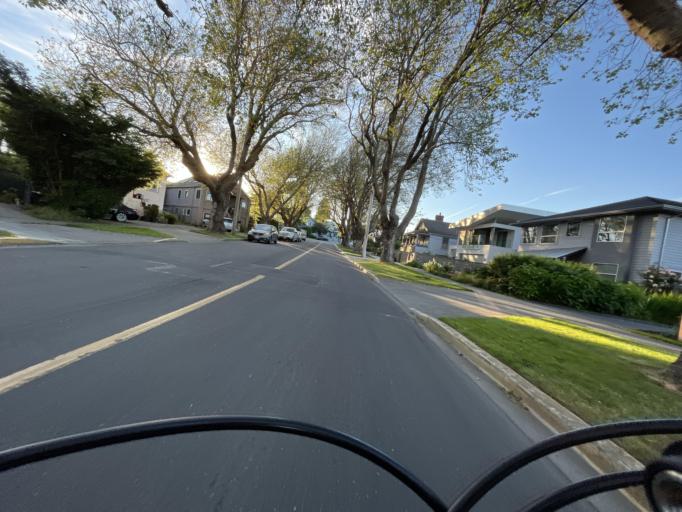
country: CA
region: British Columbia
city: Victoria
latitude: 48.4097
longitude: -123.3307
